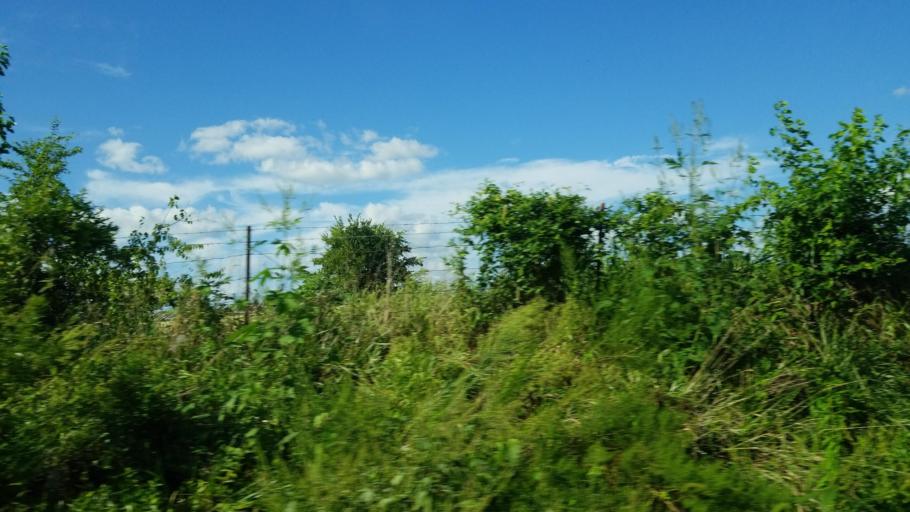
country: US
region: Illinois
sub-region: Saline County
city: Harrisburg
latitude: 37.8163
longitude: -88.5517
